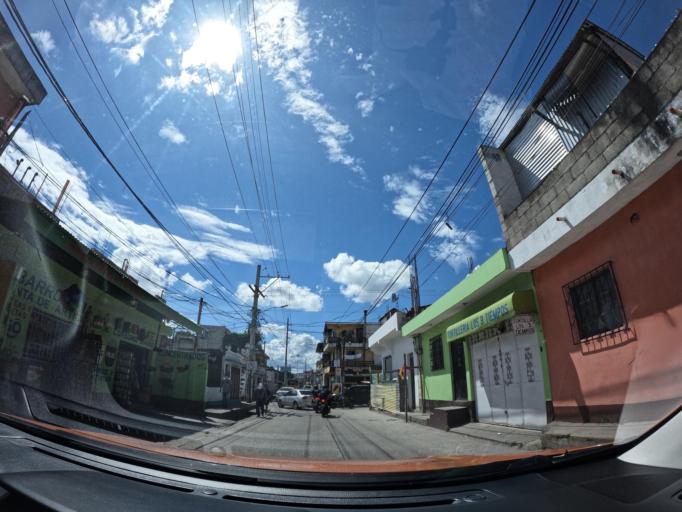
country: GT
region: Guatemala
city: Santa Catarina Pinula
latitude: 14.5531
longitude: -90.5224
